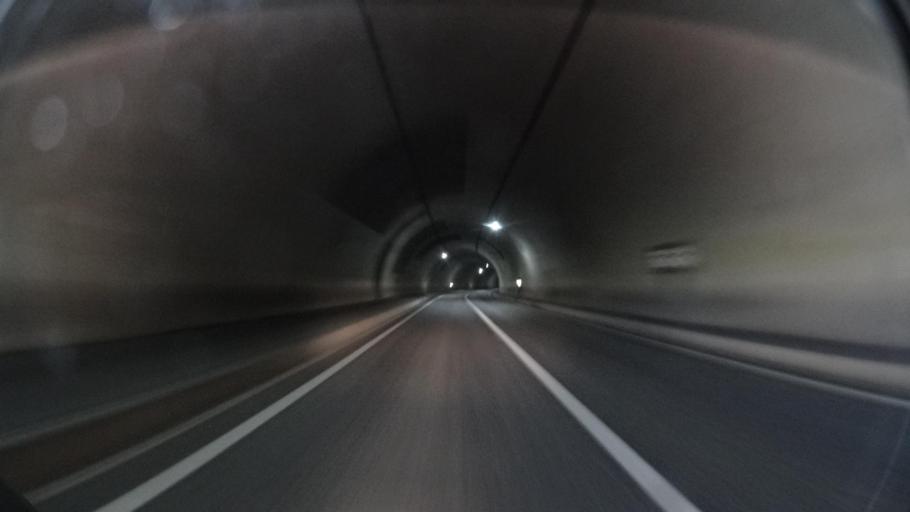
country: JP
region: Kyoto
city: Maizuru
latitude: 35.5225
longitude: 135.3498
